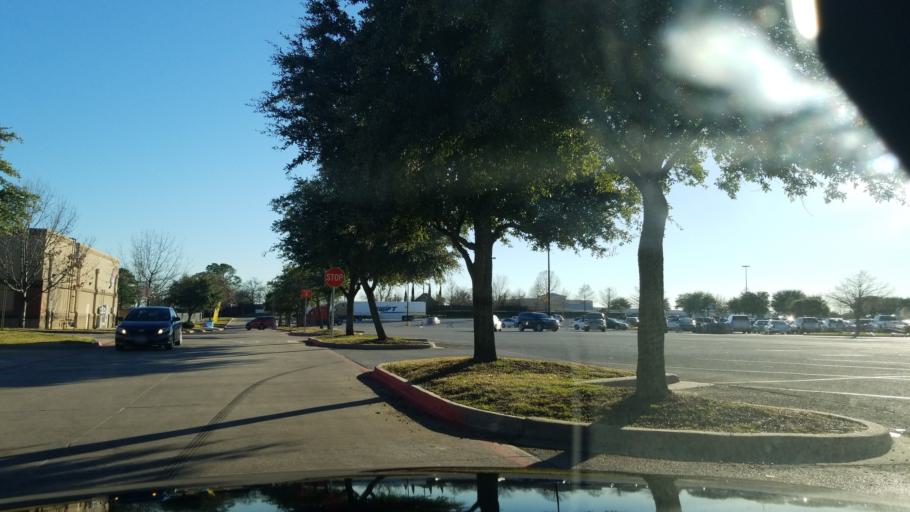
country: US
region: Texas
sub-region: Denton County
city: Hickory Creek
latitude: 33.1281
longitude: -97.0444
